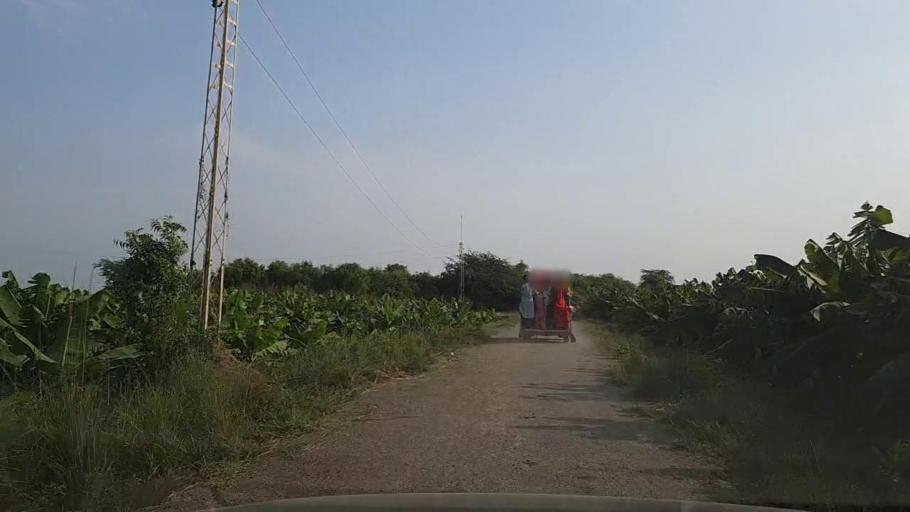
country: PK
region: Sindh
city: Thatta
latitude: 24.6411
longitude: 67.9512
